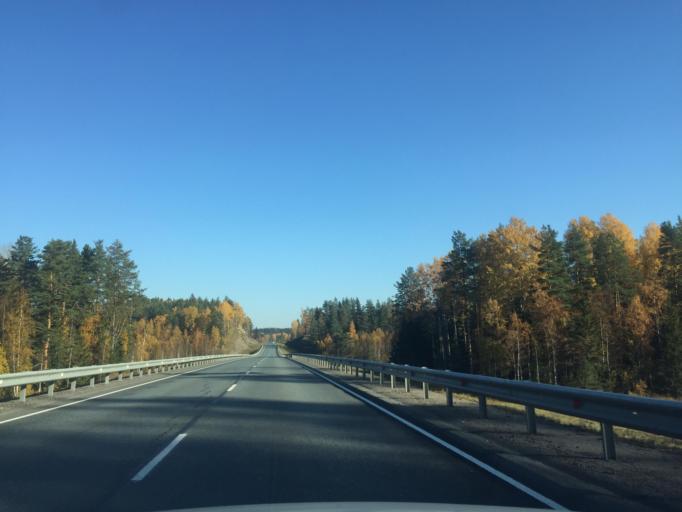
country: RU
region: Leningrad
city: Kuznechnoye
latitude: 61.3212
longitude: 29.8042
